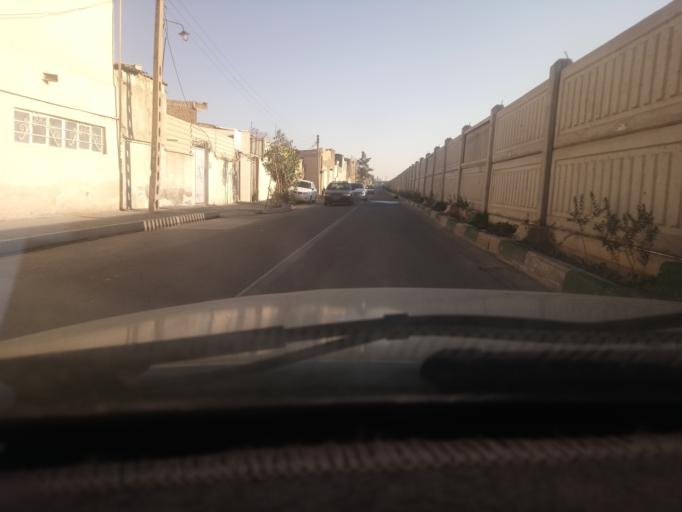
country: IR
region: Qom
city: Qom
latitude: 34.6645
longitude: 50.8678
